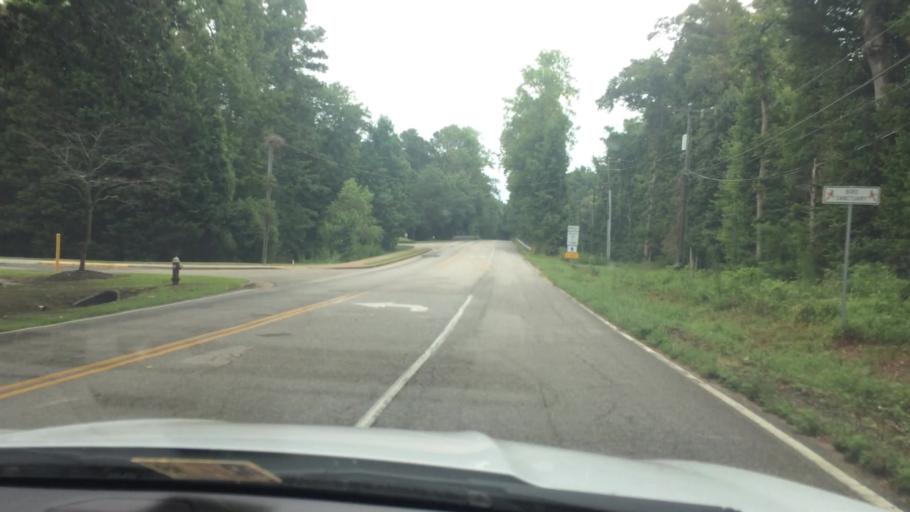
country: US
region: Virginia
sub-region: City of Williamsburg
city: Williamsburg
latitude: 37.2832
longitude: -76.6710
